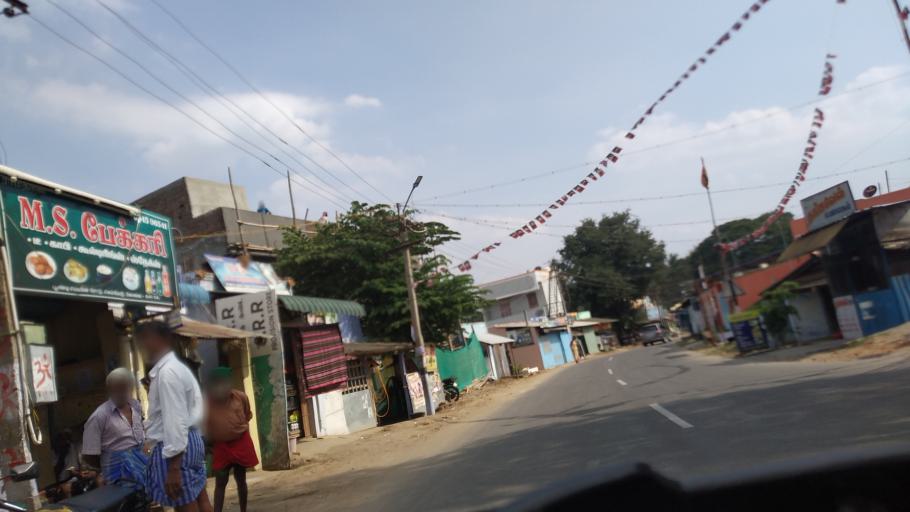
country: IN
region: Tamil Nadu
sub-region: Coimbatore
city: Perur
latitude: 10.9571
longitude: 76.7596
